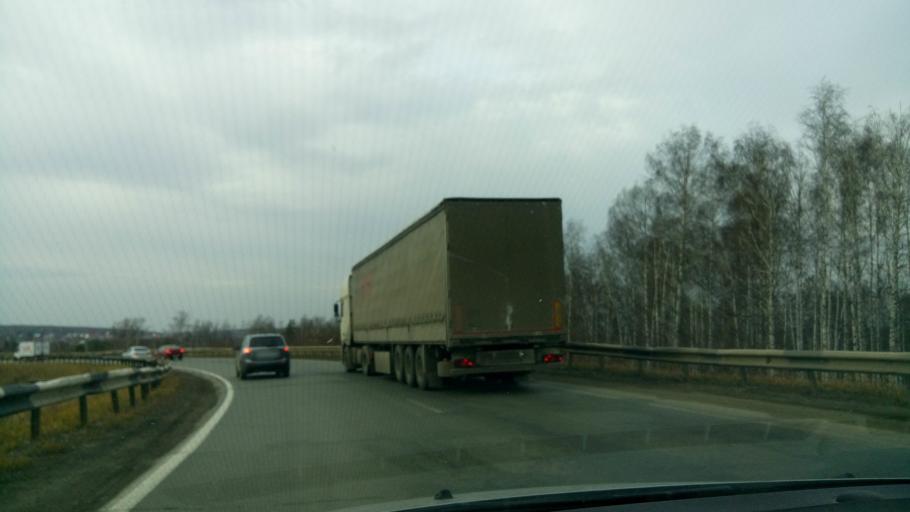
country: RU
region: Sverdlovsk
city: Verkhneye Dubrovo
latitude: 56.7381
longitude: 61.1060
